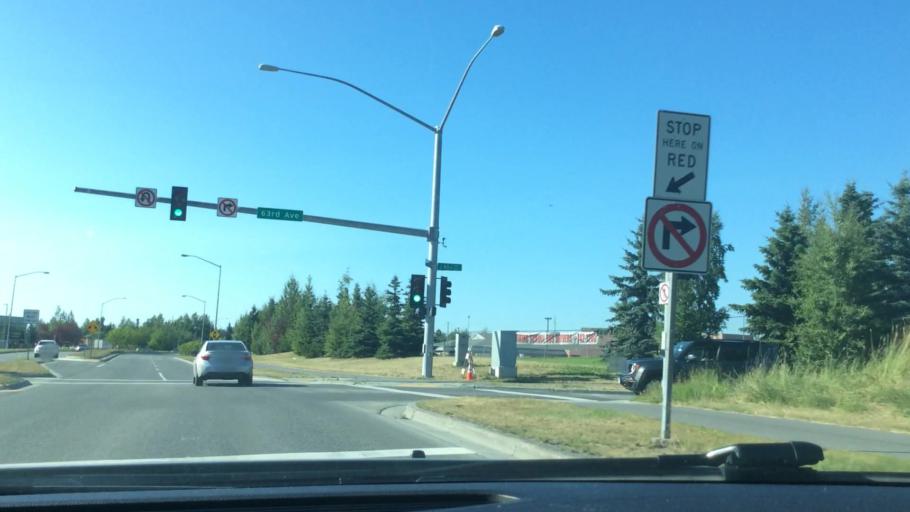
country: US
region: Alaska
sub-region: Anchorage Municipality
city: Anchorage
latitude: 61.1632
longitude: -149.8351
